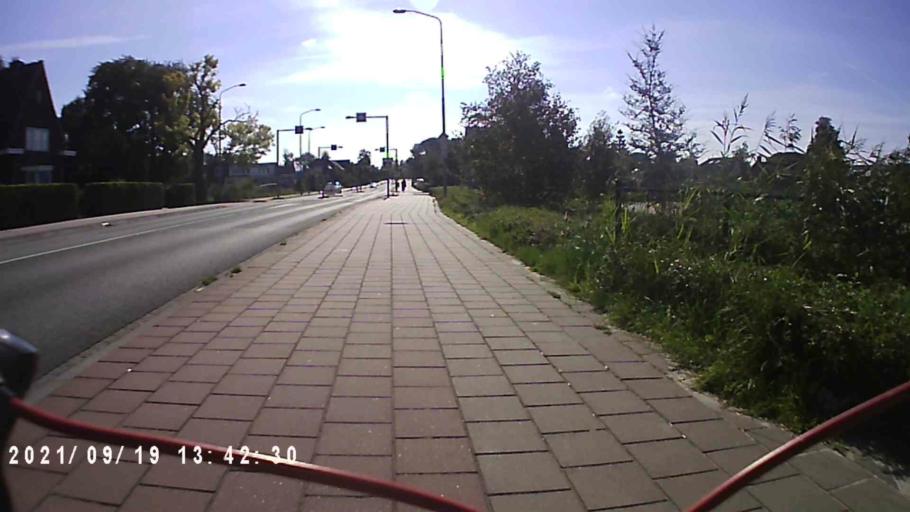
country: NL
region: Groningen
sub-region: Gemeente  Oldambt
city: Winschoten
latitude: 53.1385
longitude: 7.0415
